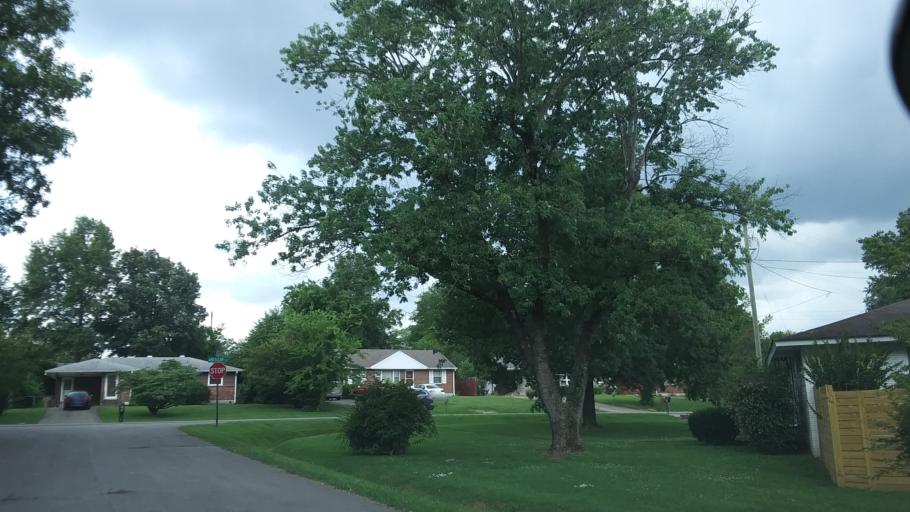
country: US
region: Tennessee
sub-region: Davidson County
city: Belle Meade
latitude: 36.1527
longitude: -86.8808
